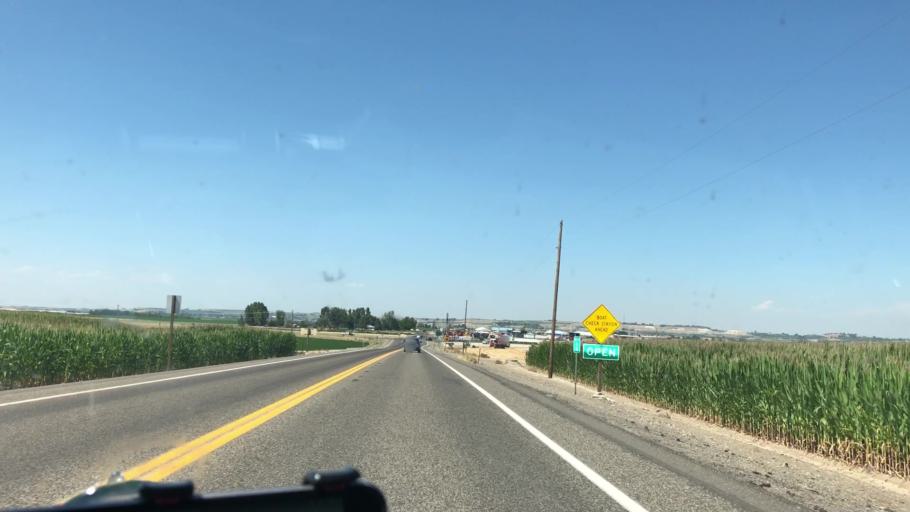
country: US
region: Idaho
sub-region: Owyhee County
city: Marsing
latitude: 43.5412
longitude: -116.8517
